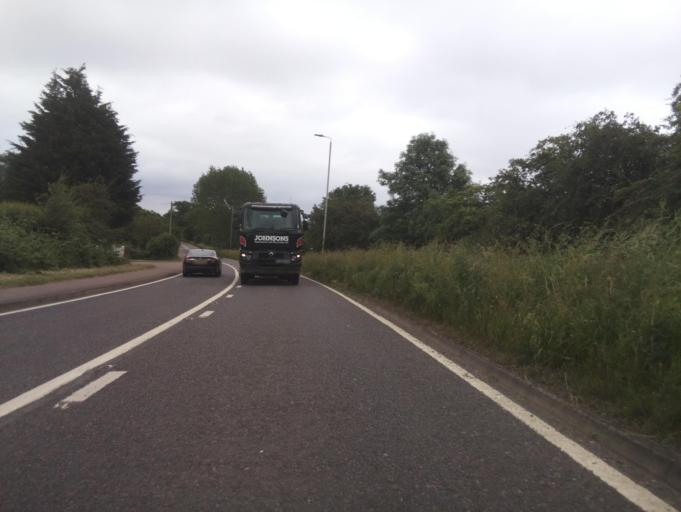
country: GB
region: England
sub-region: Leicestershire
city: Melton Mowbray
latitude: 52.7643
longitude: -0.9188
